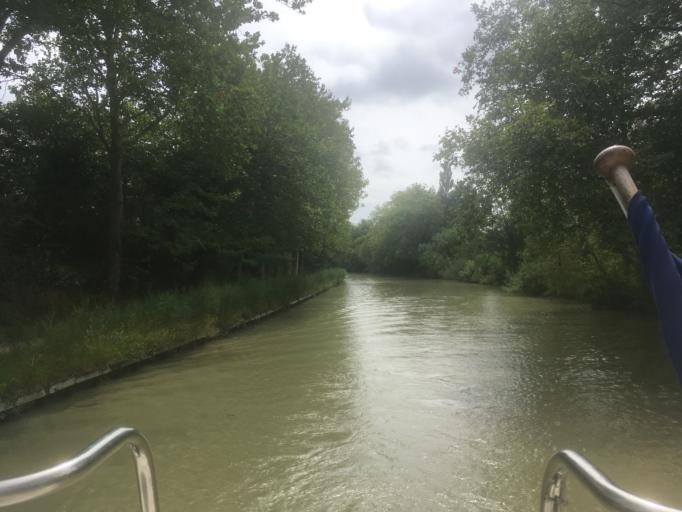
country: FR
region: Languedoc-Roussillon
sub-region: Departement de l'Aude
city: Villepinte
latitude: 43.2782
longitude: 2.0561
